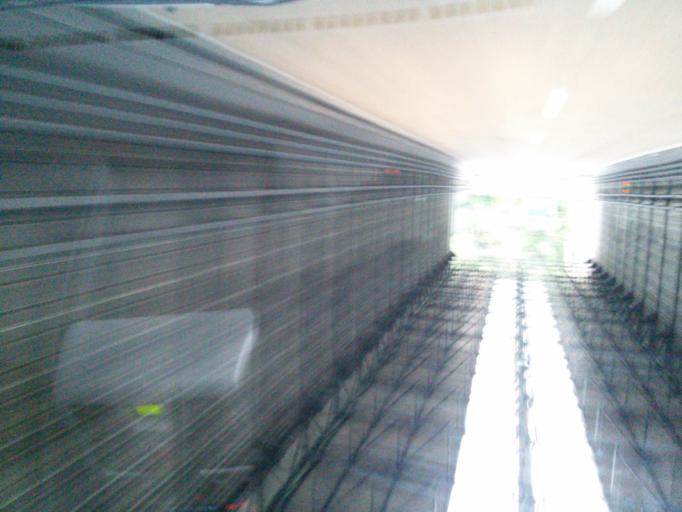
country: IT
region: Liguria
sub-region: Provincia di Genova
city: Genoa
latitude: 44.4564
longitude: 8.9040
